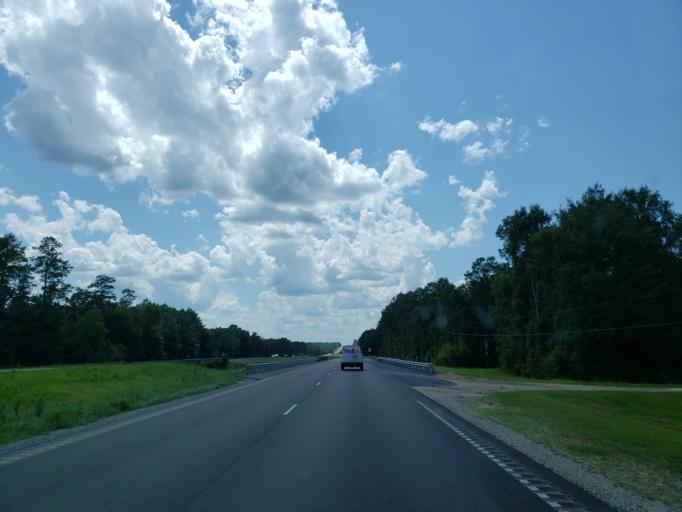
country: US
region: Mississippi
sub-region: Perry County
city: New Augusta
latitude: 31.2113
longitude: -89.1252
